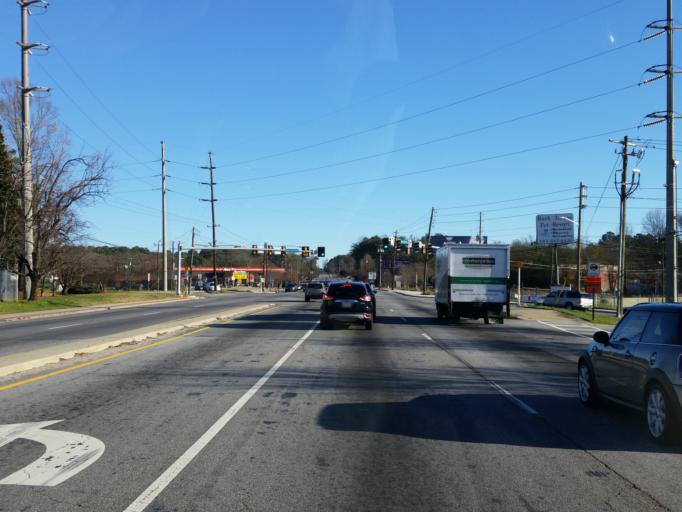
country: US
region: Georgia
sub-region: Cobb County
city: Vinings
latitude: 33.8218
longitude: -84.4557
